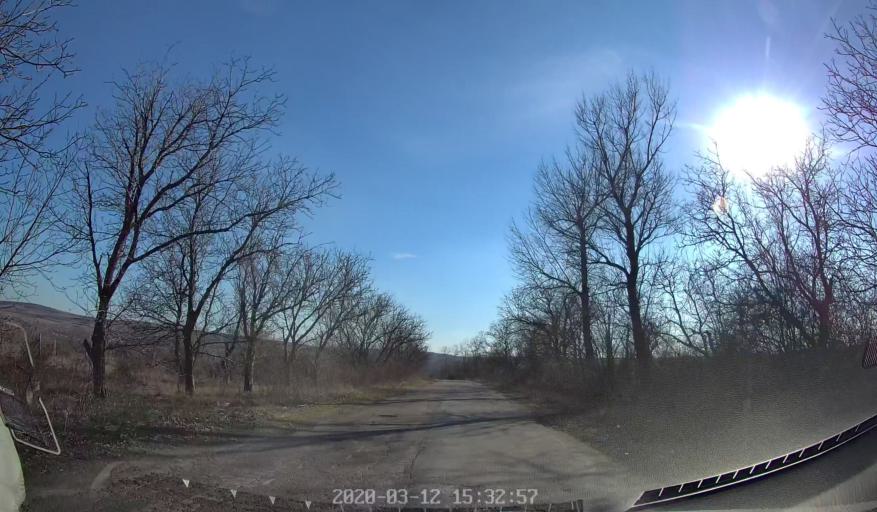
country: MD
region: Chisinau
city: Ciorescu
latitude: 47.1474
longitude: 28.9389
